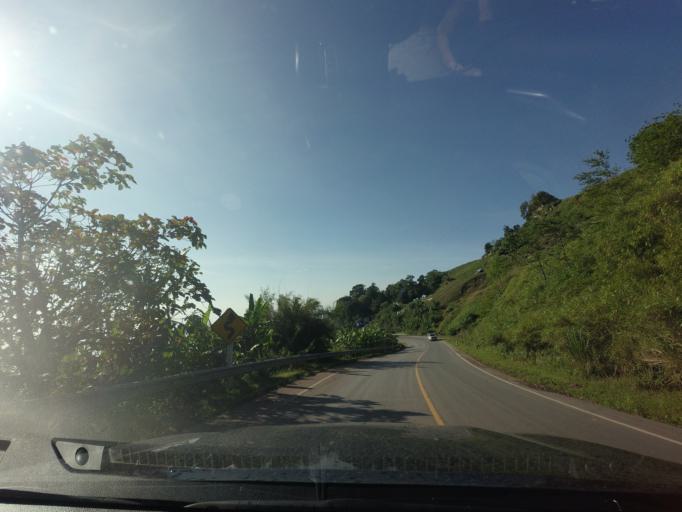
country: TH
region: Phetchabun
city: Lom Kao
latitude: 16.8828
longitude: 101.1005
